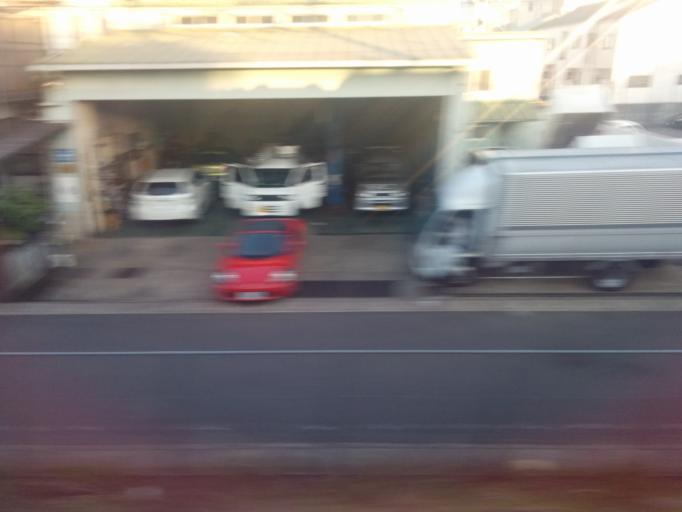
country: JP
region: Kyoto
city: Muko
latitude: 34.9721
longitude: 135.7149
